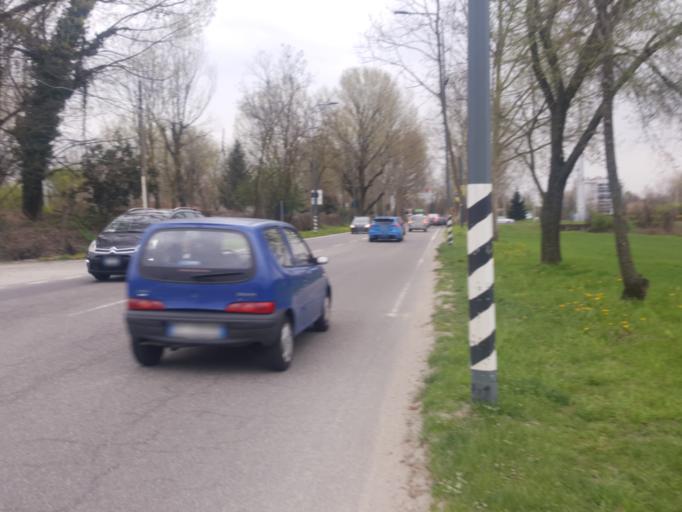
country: IT
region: Lombardy
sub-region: Citta metropolitana di Milano
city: Romano Banco
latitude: 45.4324
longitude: 9.1252
